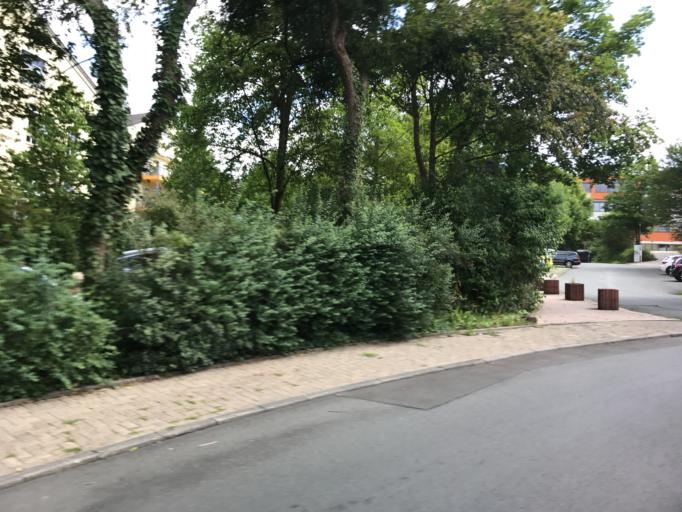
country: DE
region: Hesse
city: Weilburg
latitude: 50.4823
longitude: 8.2724
